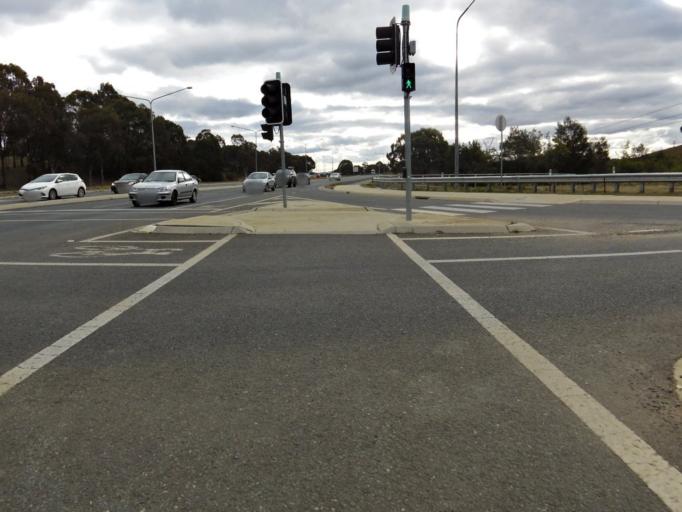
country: AU
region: Australian Capital Territory
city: Belconnen
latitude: -35.2335
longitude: 149.0874
